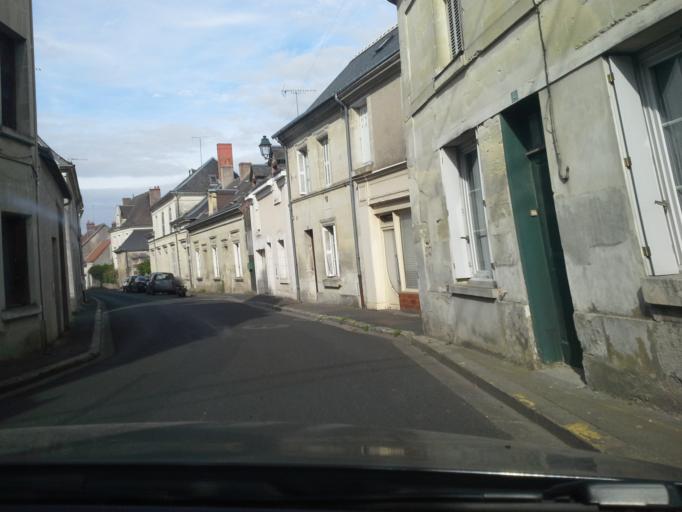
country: FR
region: Centre
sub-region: Departement d'Indre-et-Loire
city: Reugny
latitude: 47.4824
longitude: 0.8847
